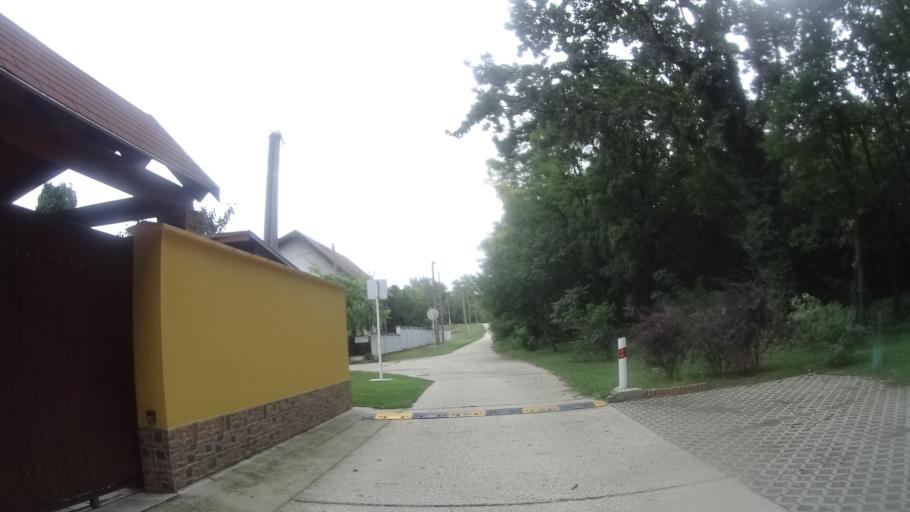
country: HU
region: Komarom-Esztergom
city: Acs
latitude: 47.7613
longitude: 18.0551
